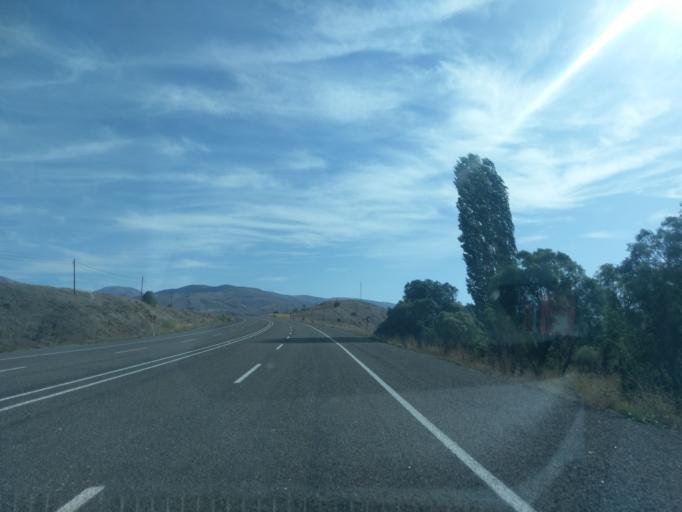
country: TR
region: Sivas
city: Imranli
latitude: 39.8352
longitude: 38.2669
